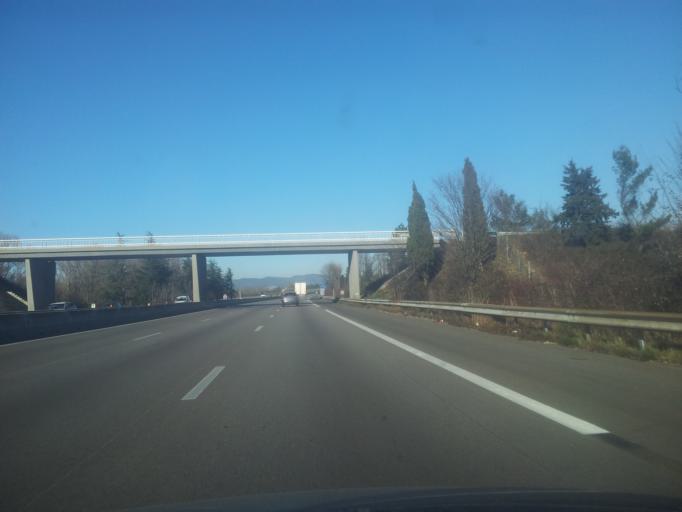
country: FR
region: Rhone-Alpes
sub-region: Departement de la Drome
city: Saulce-sur-Rhone
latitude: 44.7065
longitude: 4.7860
